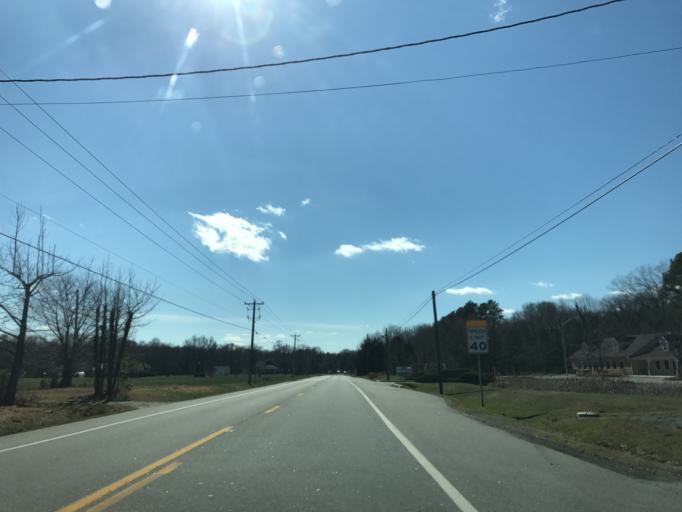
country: US
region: Maryland
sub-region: Kent County
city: Rock Hall
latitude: 39.1509
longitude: -76.2116
